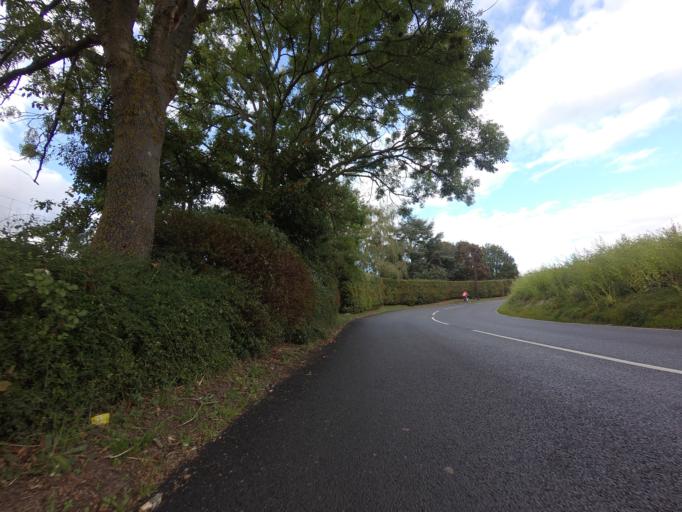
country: GB
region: England
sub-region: Kent
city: Marden
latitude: 51.2142
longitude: 0.5110
